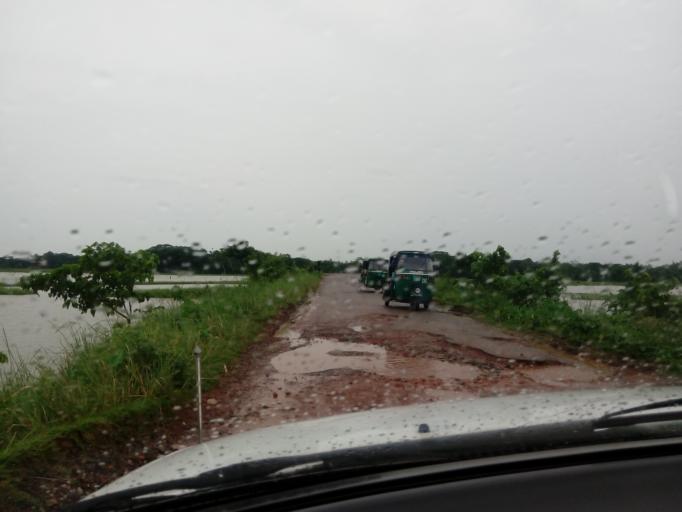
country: BD
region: Sylhet
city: Sylhet
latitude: 24.9616
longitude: 91.7960
